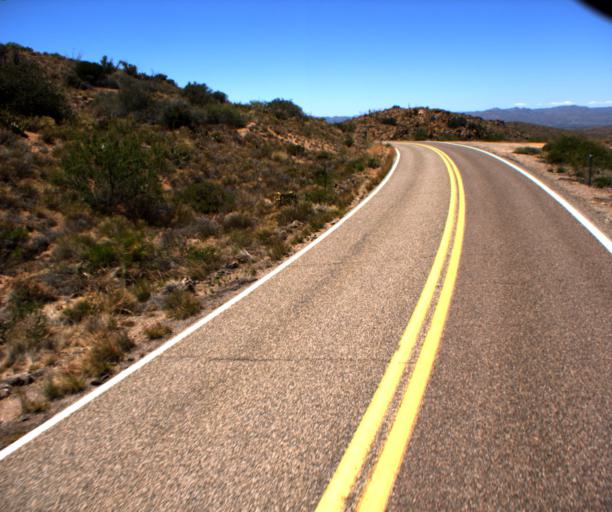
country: US
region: Arizona
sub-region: Yavapai County
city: Bagdad
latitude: 34.4458
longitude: -112.9656
